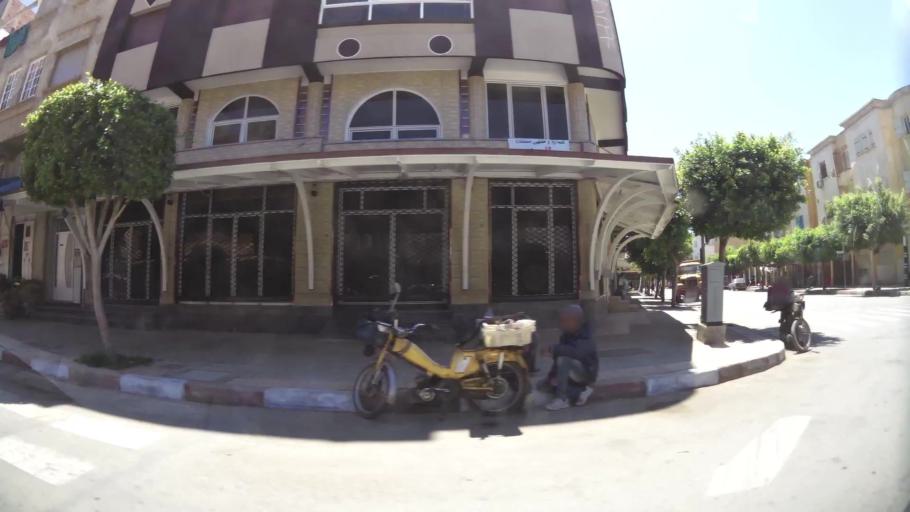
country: MA
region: Oriental
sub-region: Berkane-Taourirt
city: Madagh
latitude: 35.0783
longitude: -2.2255
